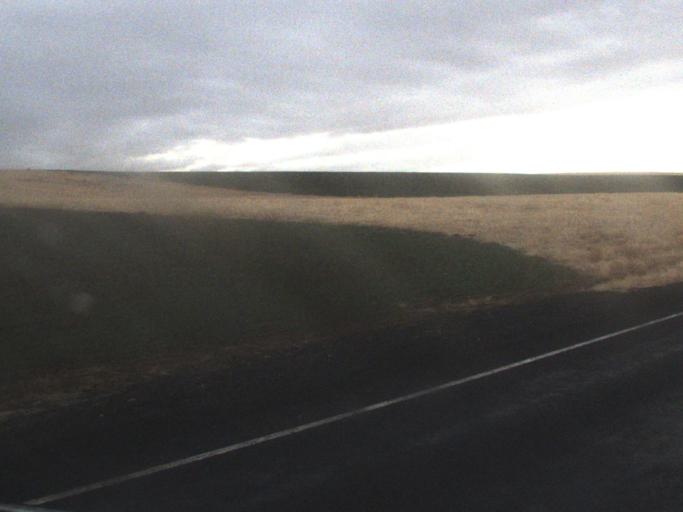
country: US
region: Washington
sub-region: Lincoln County
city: Davenport
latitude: 47.7165
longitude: -118.1515
